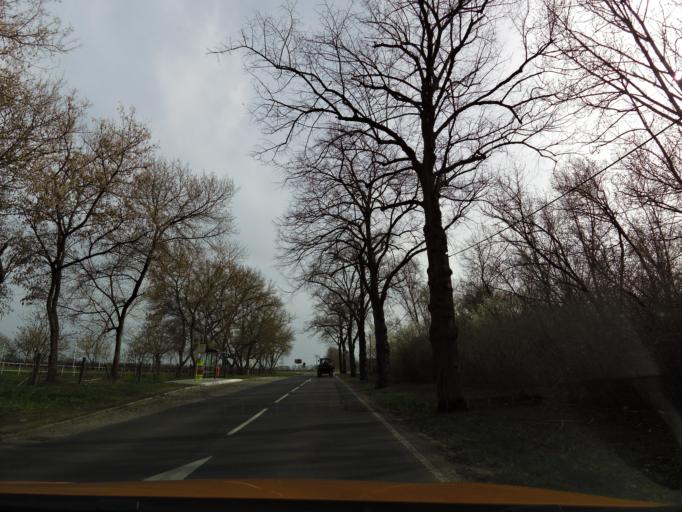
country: DE
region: Brandenburg
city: Grossbeeren
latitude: 52.3495
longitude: 13.2748
